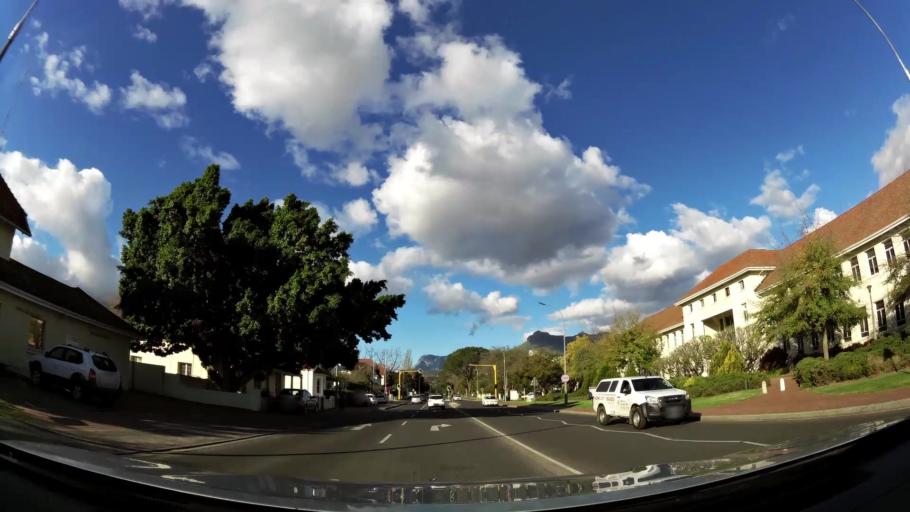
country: ZA
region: Western Cape
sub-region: Cape Winelands District Municipality
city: Stellenbosch
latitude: -33.9313
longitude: 18.8667
